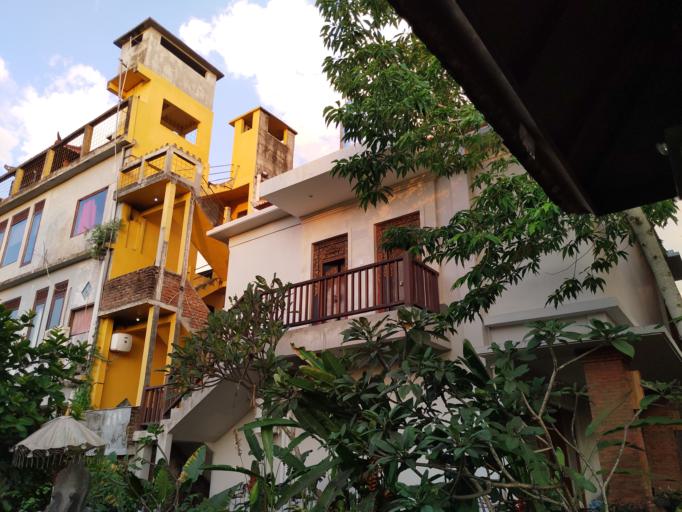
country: ID
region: Bali
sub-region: Kabupaten Gianyar
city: Ubud
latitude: -8.5109
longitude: 115.2605
